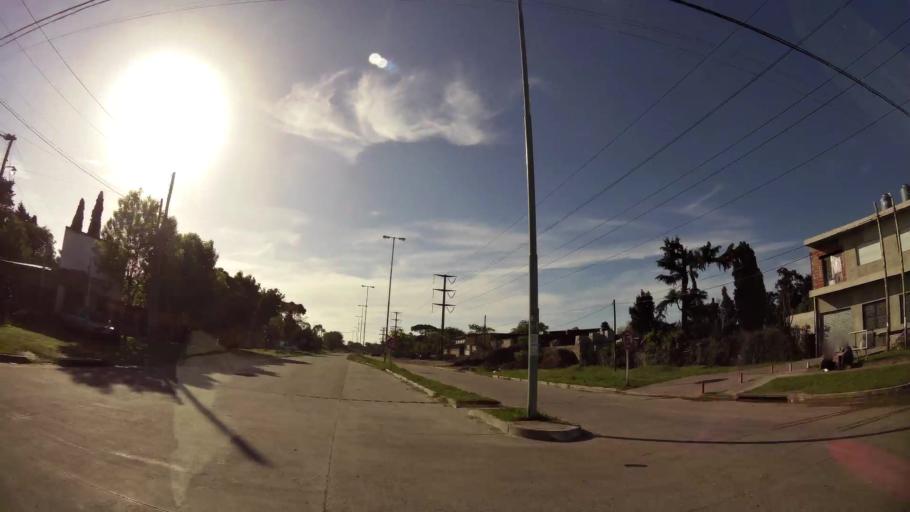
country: AR
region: Buenos Aires
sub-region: Partido de Quilmes
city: Quilmes
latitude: -34.8106
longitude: -58.2107
